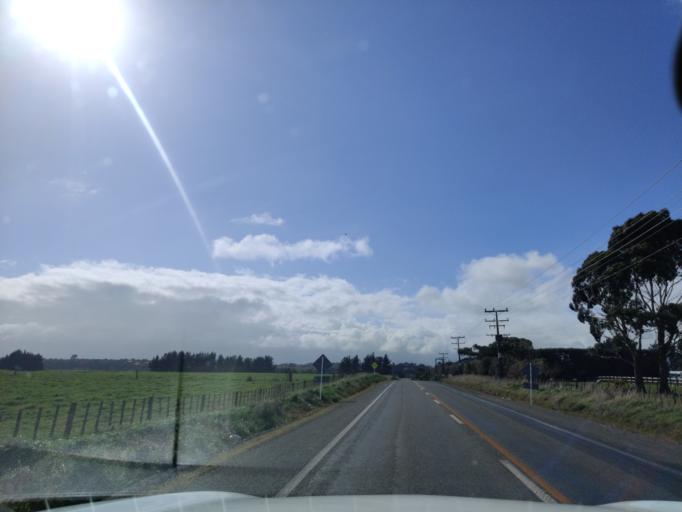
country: NZ
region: Manawatu-Wanganui
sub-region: Palmerston North City
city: Palmerston North
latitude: -40.3985
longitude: 175.6233
